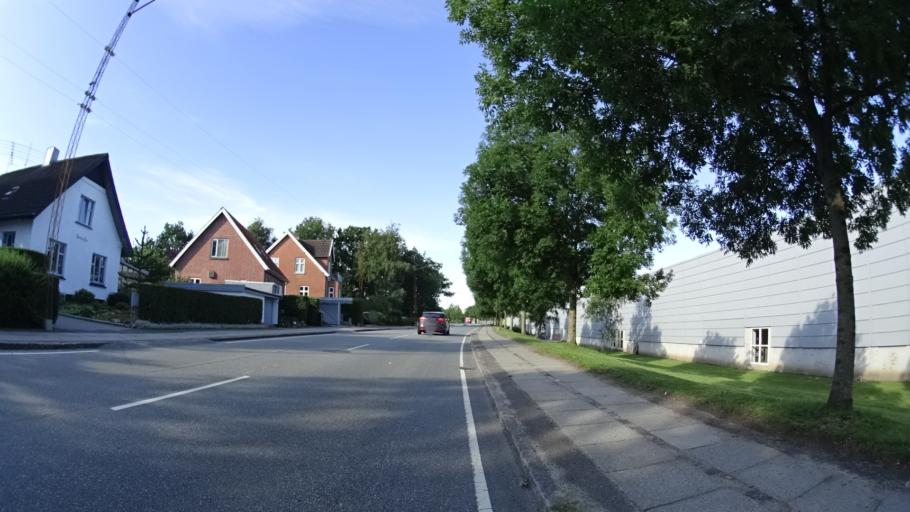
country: DK
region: Central Jutland
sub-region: Arhus Kommune
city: Stavtrup
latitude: 56.1166
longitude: 10.1560
